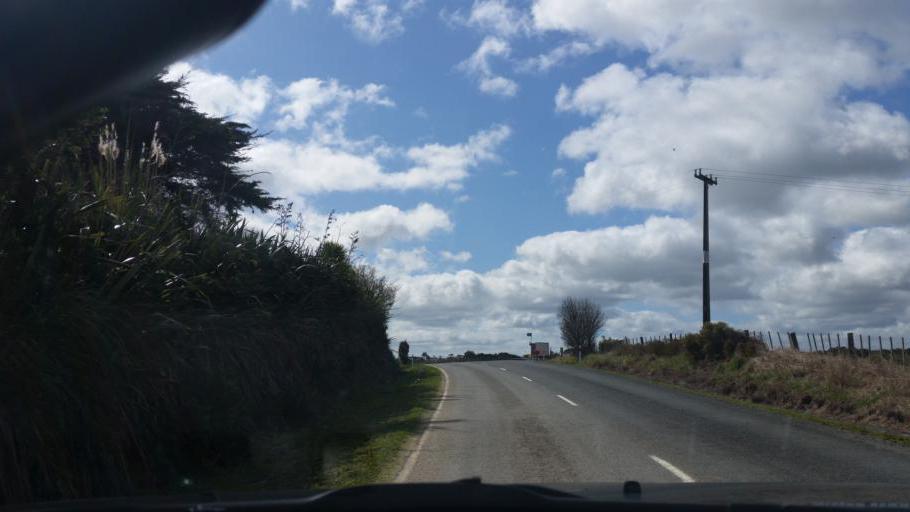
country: NZ
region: Auckland
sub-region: Auckland
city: Wellsford
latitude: -36.1534
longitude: 174.4998
